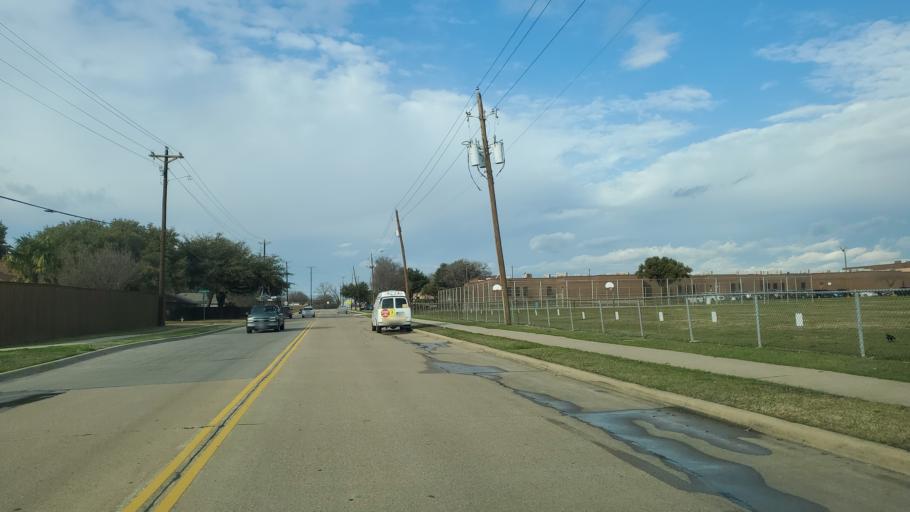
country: US
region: Texas
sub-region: Dallas County
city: Carrollton
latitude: 33.0019
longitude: -96.8985
